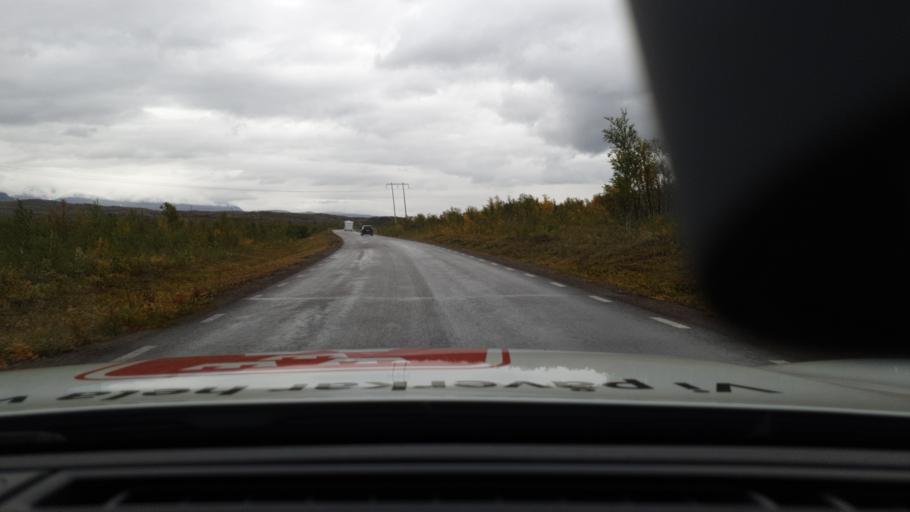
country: NO
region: Troms
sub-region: Bardu
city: Setermoen
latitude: 68.4268
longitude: 18.3881
